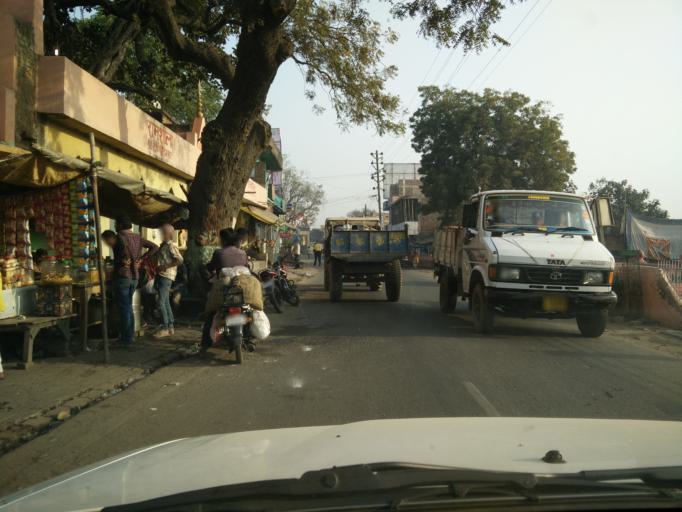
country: IN
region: Bihar
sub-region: Gaya
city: Gaya
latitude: 24.8121
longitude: 85.0155
